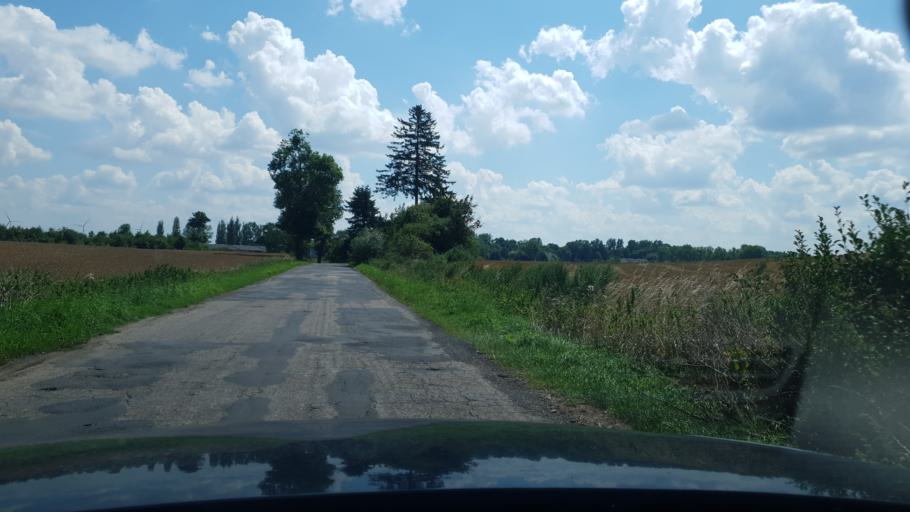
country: PL
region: Kujawsko-Pomorskie
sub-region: Powiat wabrzeski
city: Pluznica
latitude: 53.3521
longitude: 18.8253
